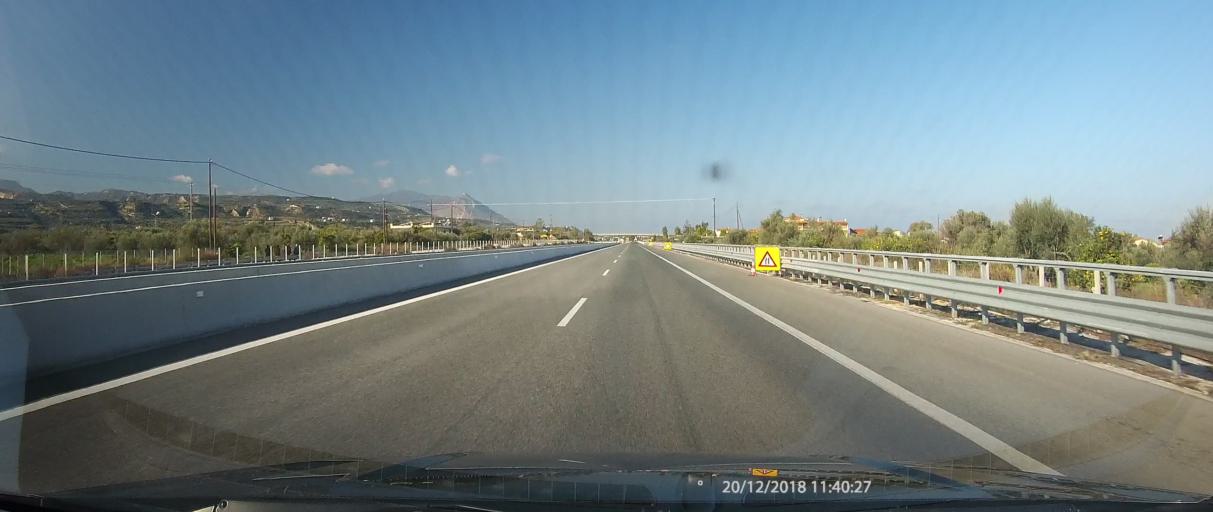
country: GR
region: Peloponnese
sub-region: Nomos Korinthias
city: Xylokastro
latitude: 38.0531
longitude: 22.6776
